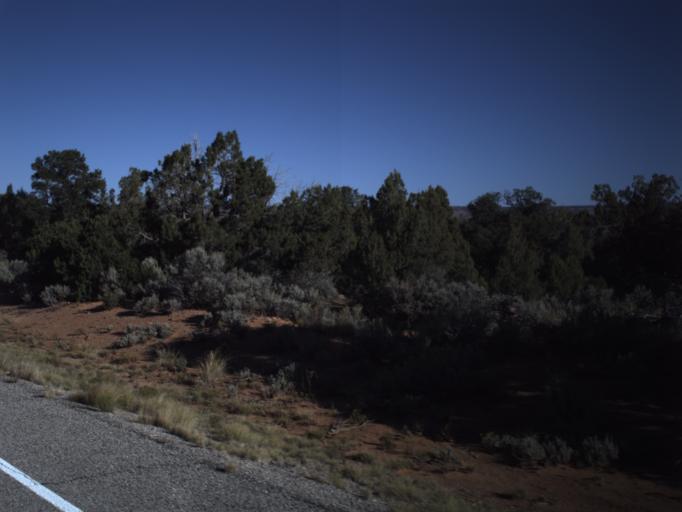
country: US
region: Utah
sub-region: San Juan County
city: Blanding
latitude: 37.5544
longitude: -109.9970
